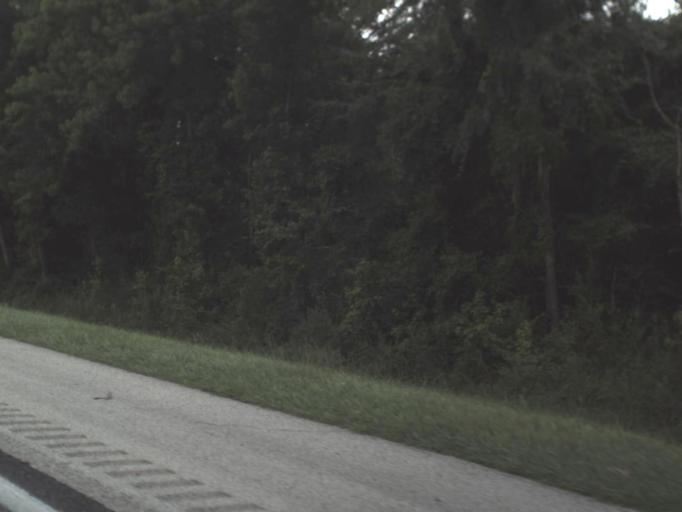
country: US
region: Florida
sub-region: Alachua County
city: Gainesville
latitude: 29.5531
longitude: -82.3412
